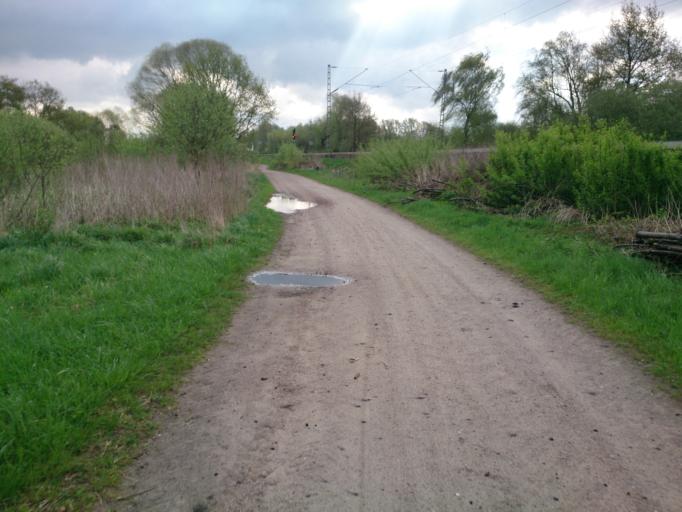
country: DE
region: Lower Saxony
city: Neu Wulmstorf
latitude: 53.4743
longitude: 9.8097
